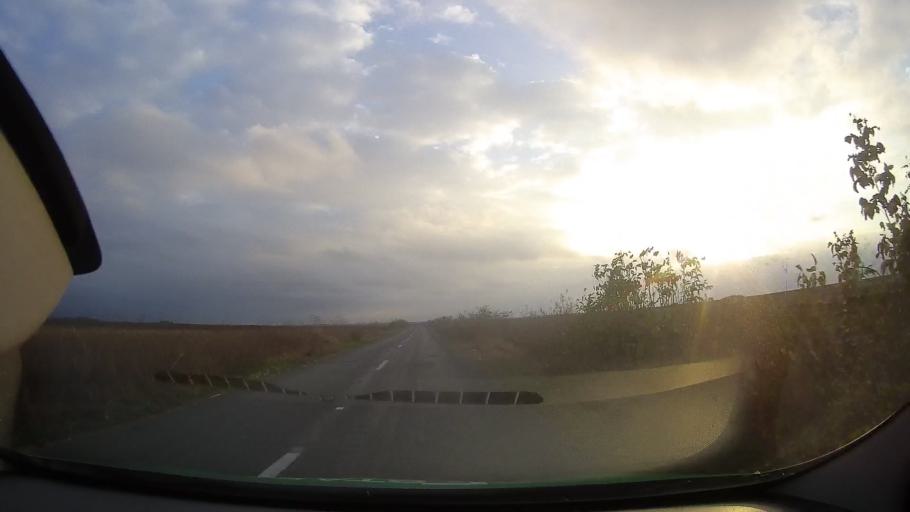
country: RO
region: Constanta
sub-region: Comuna Adamclisi
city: Adamclisi
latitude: 44.0233
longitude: 27.9079
